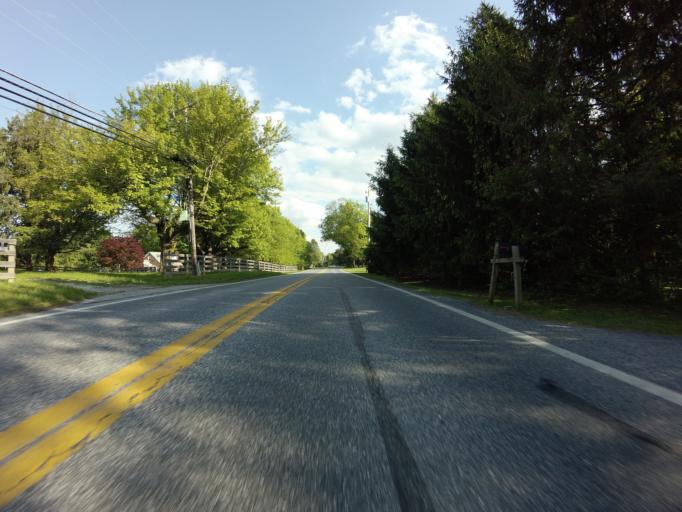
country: US
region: Maryland
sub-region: Baltimore County
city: Cockeysville
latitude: 39.4729
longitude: -76.7040
